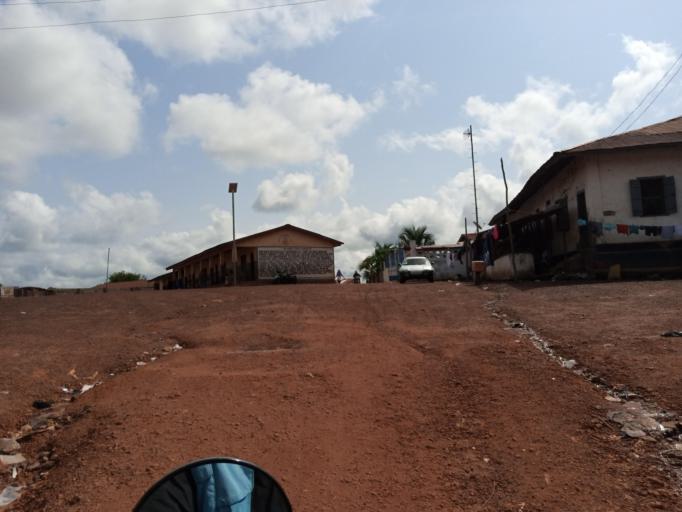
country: SL
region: Southern Province
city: Bo
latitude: 7.9717
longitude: -11.7344
